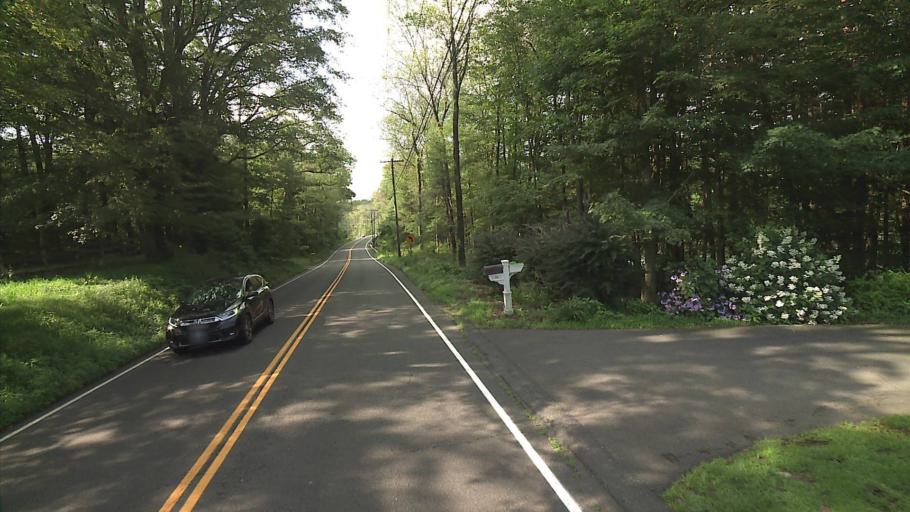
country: US
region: Connecticut
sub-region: Middlesex County
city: Higganum
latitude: 41.4151
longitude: -72.5637
